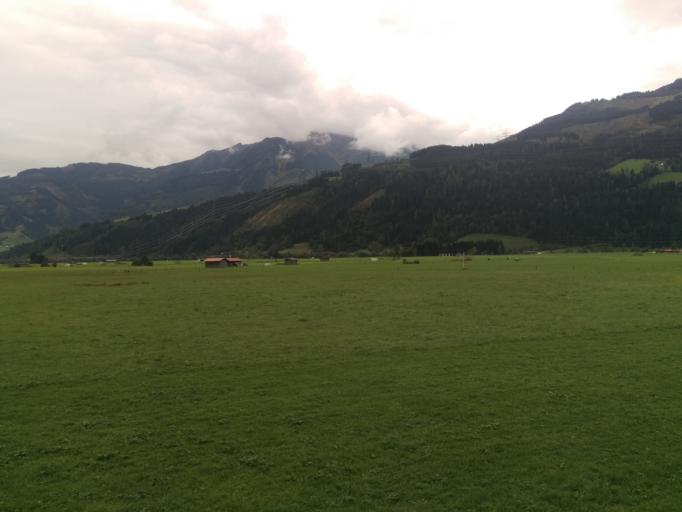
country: AT
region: Salzburg
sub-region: Politischer Bezirk Zell am See
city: Piesendorf
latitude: 47.2880
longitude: 12.7183
